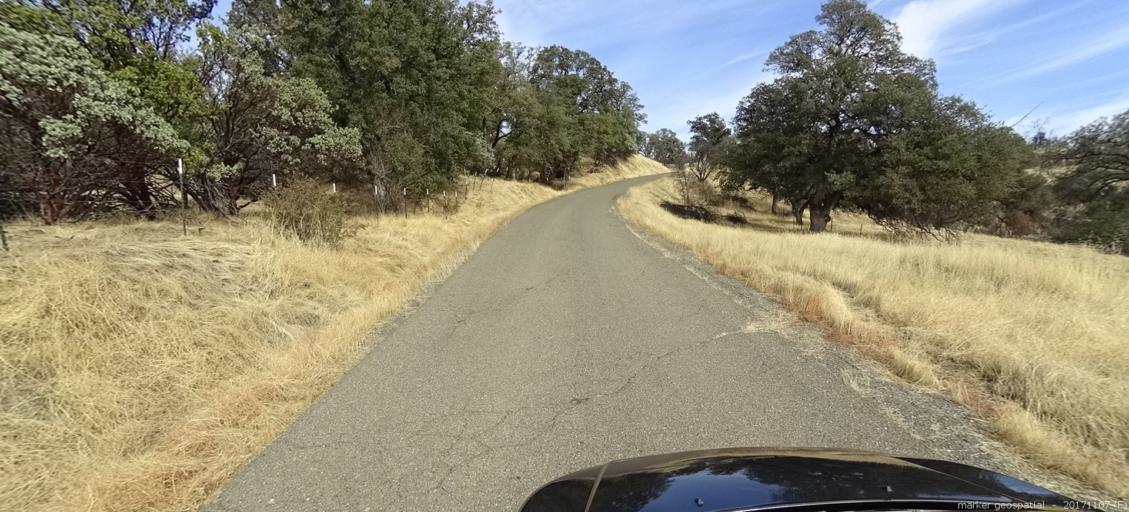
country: US
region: California
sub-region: Shasta County
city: Shasta
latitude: 40.4669
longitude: -122.5480
